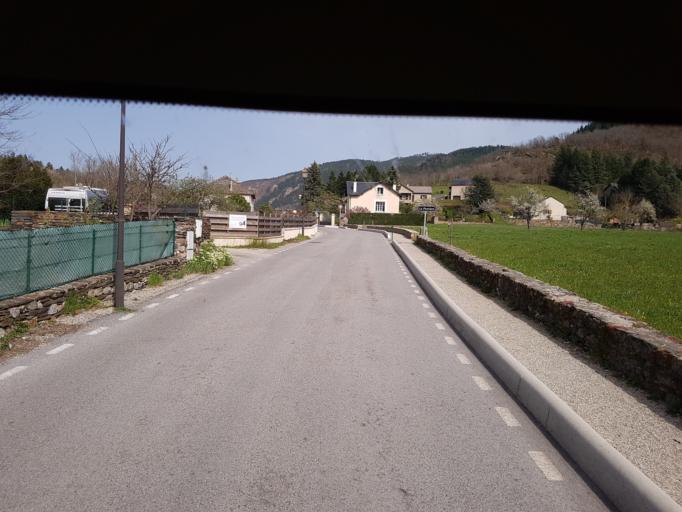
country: FR
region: Languedoc-Roussillon
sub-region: Departement de la Lozere
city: Florac
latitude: 44.3443
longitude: 3.6061
